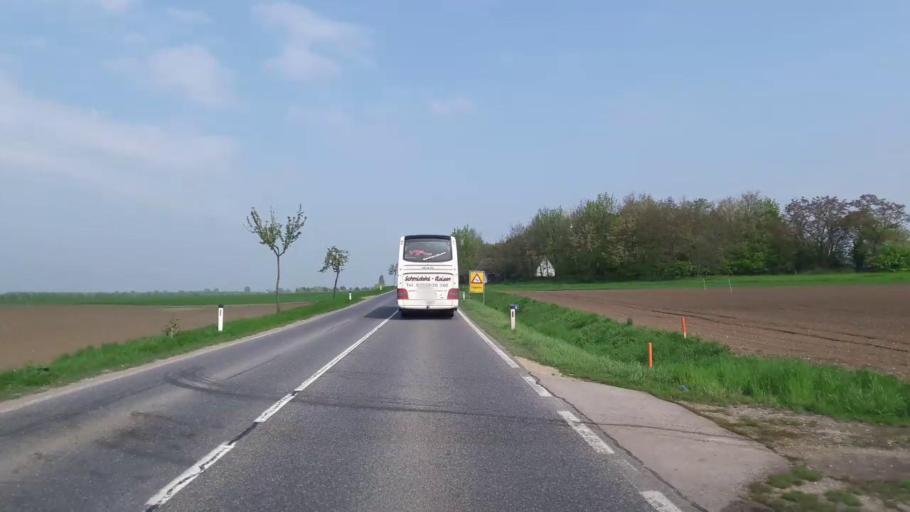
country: AT
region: Lower Austria
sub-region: Politischer Bezirk Hollabrunn
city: Guntersdorf
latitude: 48.6378
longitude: 16.0558
